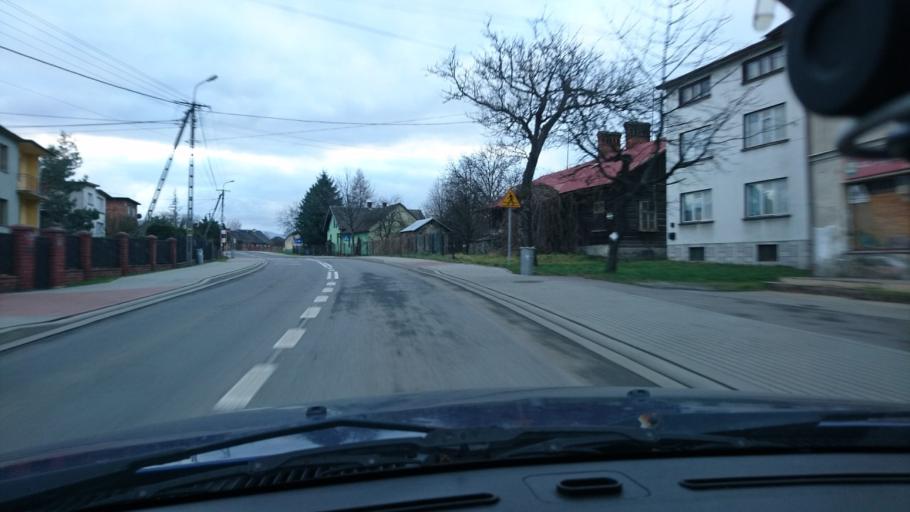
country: PL
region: Silesian Voivodeship
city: Janowice
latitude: 49.8689
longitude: 19.0938
